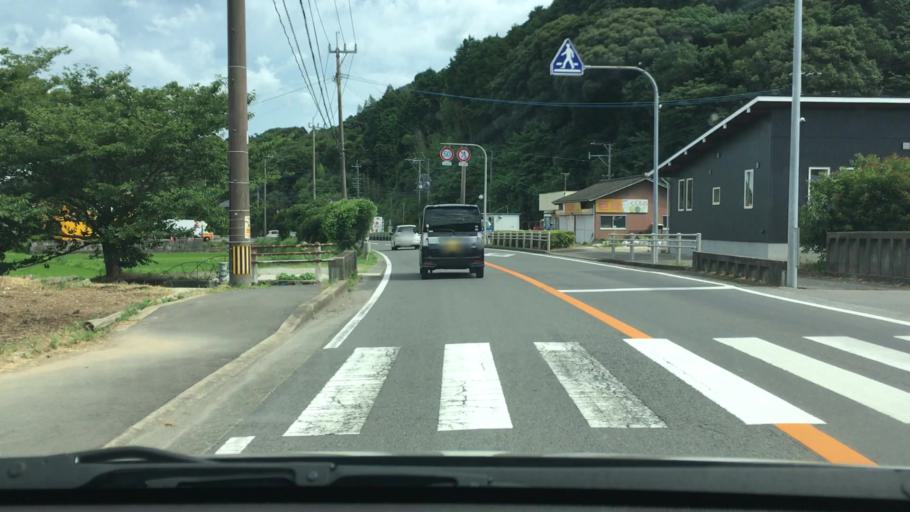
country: JP
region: Nagasaki
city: Togitsu
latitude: 32.8925
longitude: 129.7809
